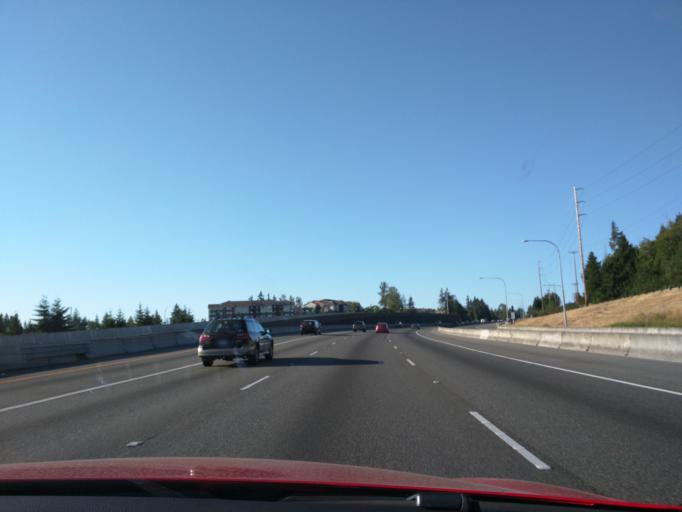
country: US
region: Washington
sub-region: Snohomish County
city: Martha Lake
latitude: 47.8501
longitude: -122.2572
